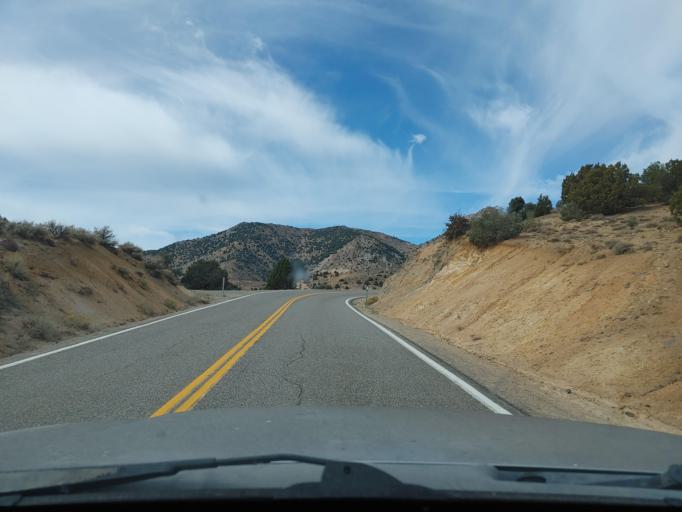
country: US
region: Nevada
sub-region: Storey County
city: Virginia City
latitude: 39.2898
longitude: -119.6415
